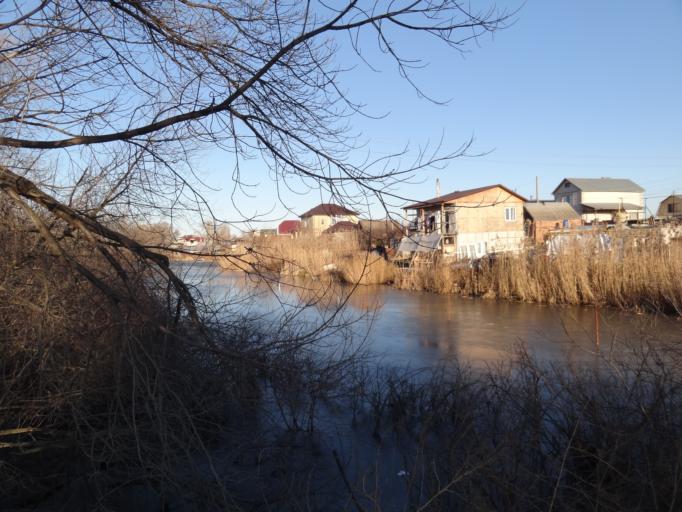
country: RU
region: Saratov
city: Engel's
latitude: 51.4983
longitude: 46.0621
